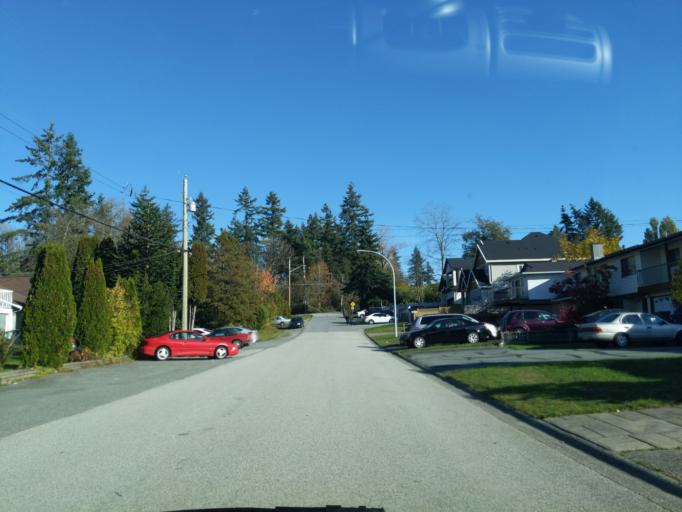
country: CA
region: British Columbia
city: New Westminster
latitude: 49.1936
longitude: -122.8671
